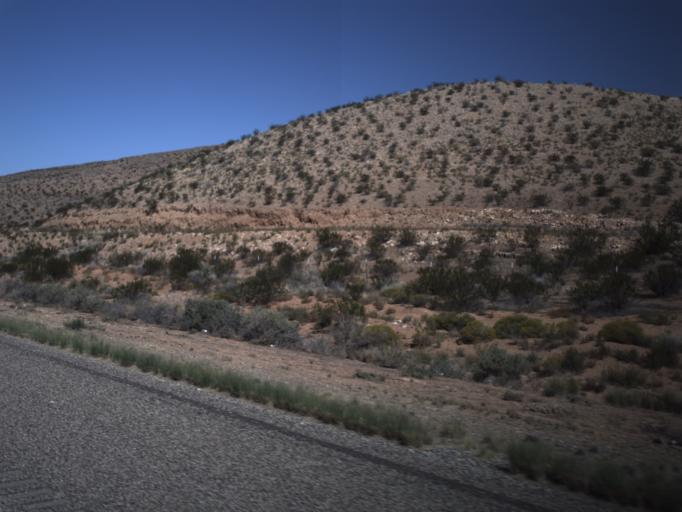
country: US
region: Utah
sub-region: Washington County
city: Saint George
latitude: 37.0130
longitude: -113.5921
